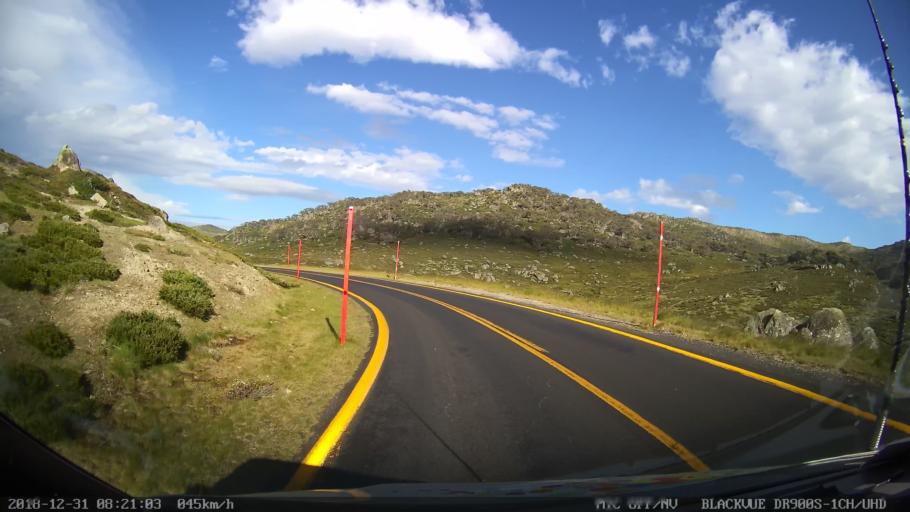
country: AU
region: New South Wales
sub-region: Snowy River
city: Jindabyne
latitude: -36.4260
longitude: 148.3704
